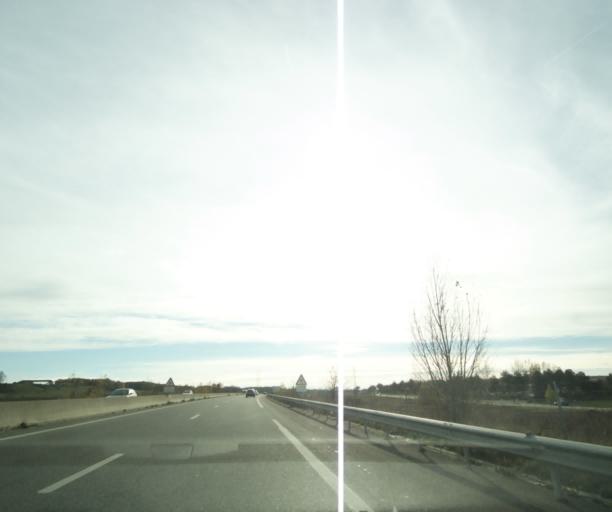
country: FR
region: Midi-Pyrenees
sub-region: Departement de la Haute-Garonne
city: La Salvetat-Saint-Gilles
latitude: 43.5977
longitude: 1.2784
